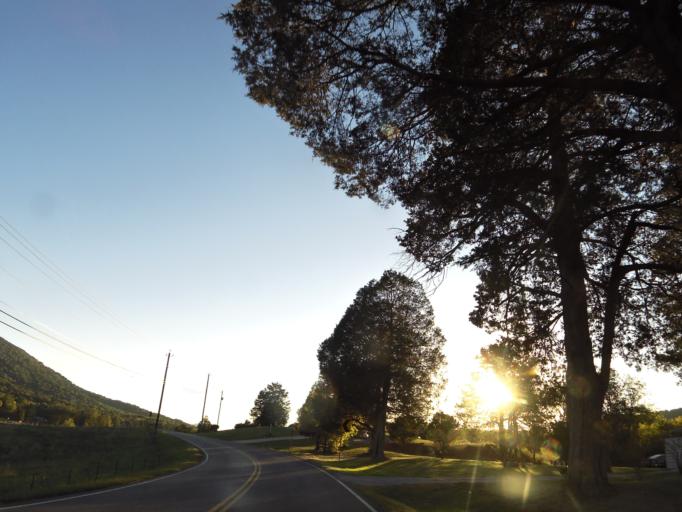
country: US
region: Tennessee
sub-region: Grainger County
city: Rutledge
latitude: 36.2795
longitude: -83.6217
